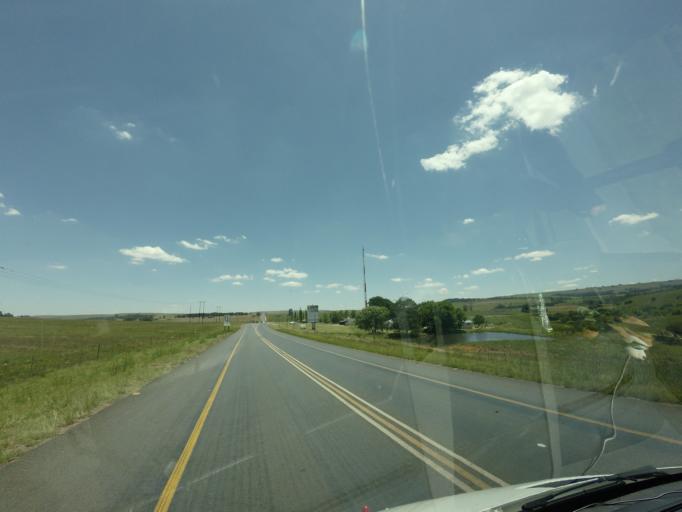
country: ZA
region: Mpumalanga
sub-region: Nkangala District Municipality
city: Belfast
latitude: -25.6871
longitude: 30.2163
